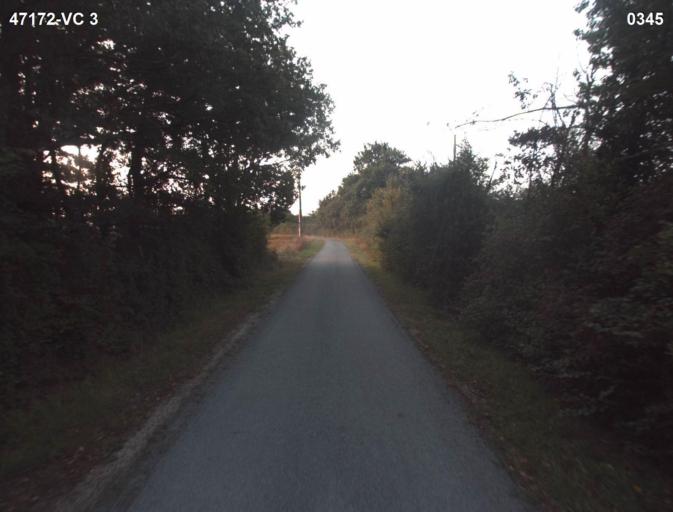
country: FR
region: Aquitaine
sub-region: Departement du Lot-et-Garonne
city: Sainte-Colombe-en-Bruilhois
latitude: 44.1669
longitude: 0.4929
